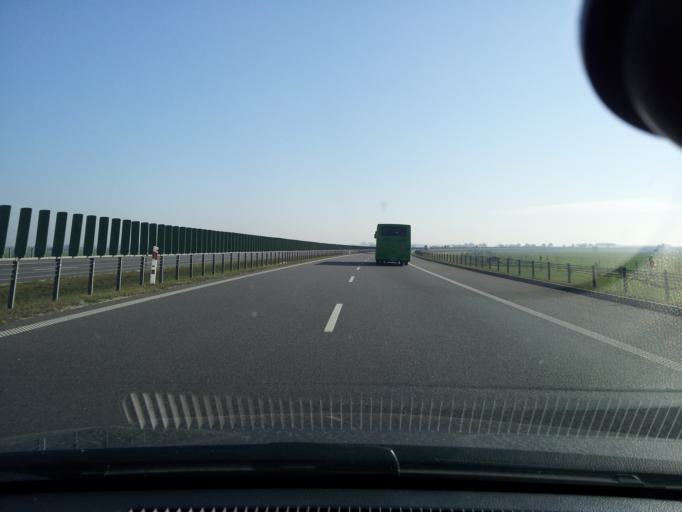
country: PL
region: Kujawsko-Pomorskie
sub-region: Grudziadz
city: Grudziadz
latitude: 53.4553
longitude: 18.6501
